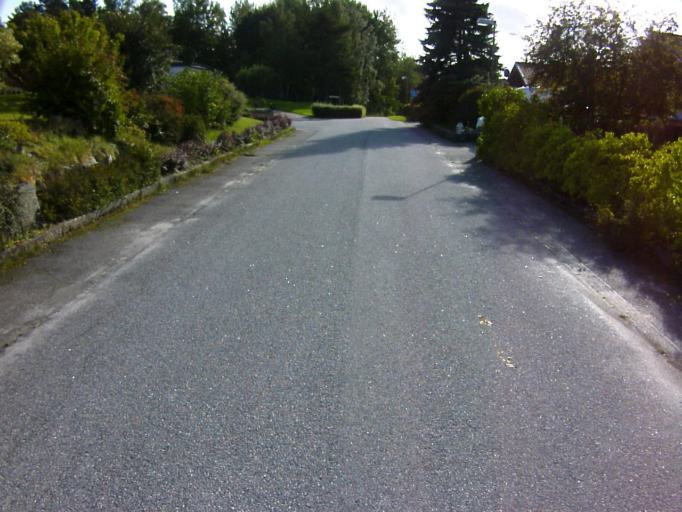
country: SE
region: Soedermanland
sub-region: Eskilstuna Kommun
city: Eskilstuna
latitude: 59.3920
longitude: 16.5424
